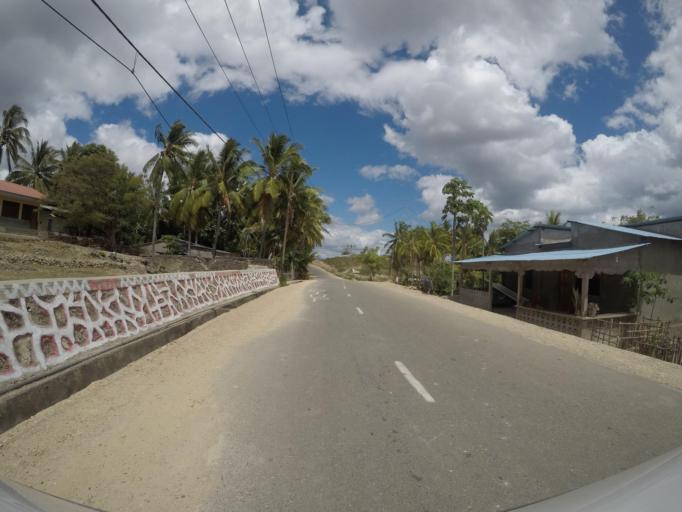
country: TL
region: Lautem
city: Lospalos
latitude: -8.3611
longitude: 126.9302
